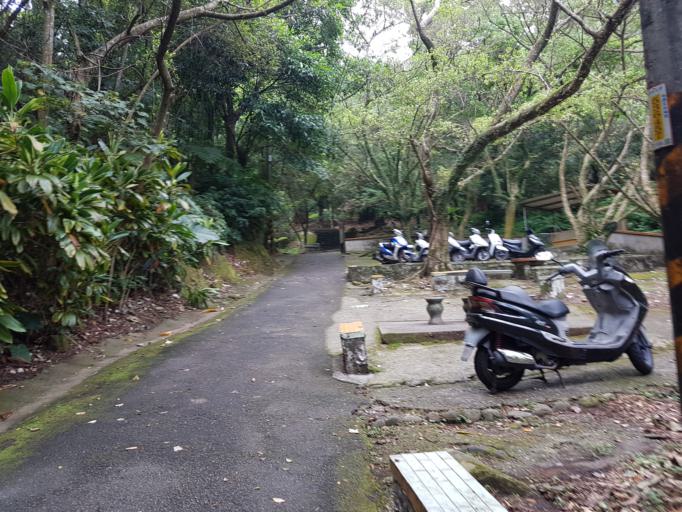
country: TW
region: Taiwan
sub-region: Keelung
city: Keelung
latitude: 25.0576
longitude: 121.6624
